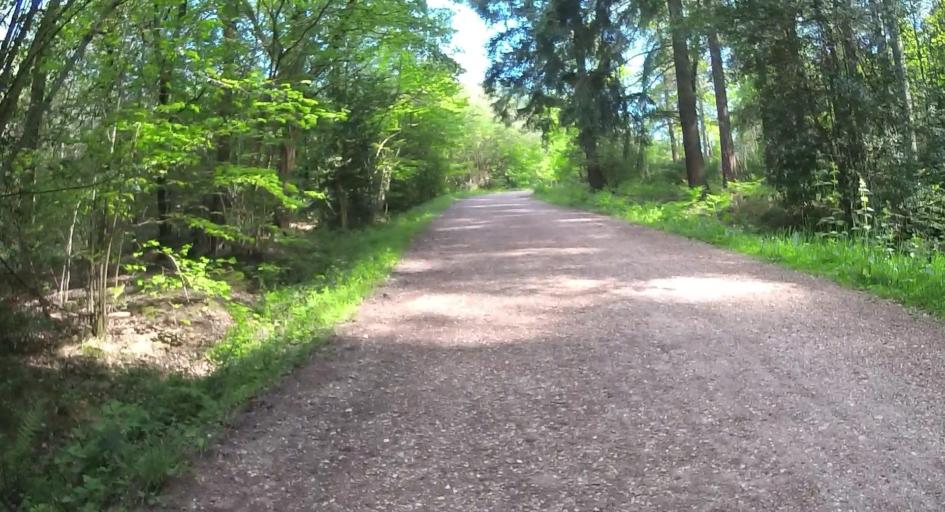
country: GB
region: England
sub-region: Hampshire
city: Lindford
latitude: 51.1664
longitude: -0.8329
